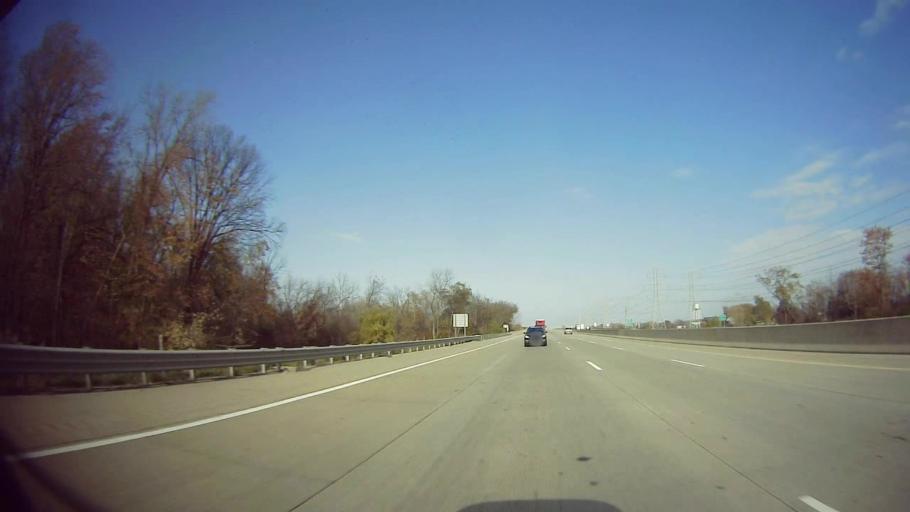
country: US
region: Michigan
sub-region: Monroe County
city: South Rockwood
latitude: 42.0673
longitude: -83.2549
